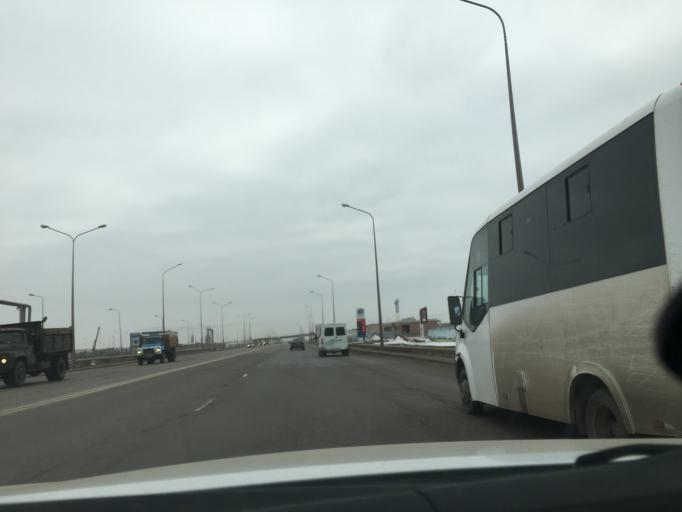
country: KZ
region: Astana Qalasy
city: Astana
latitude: 51.1576
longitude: 71.5258
